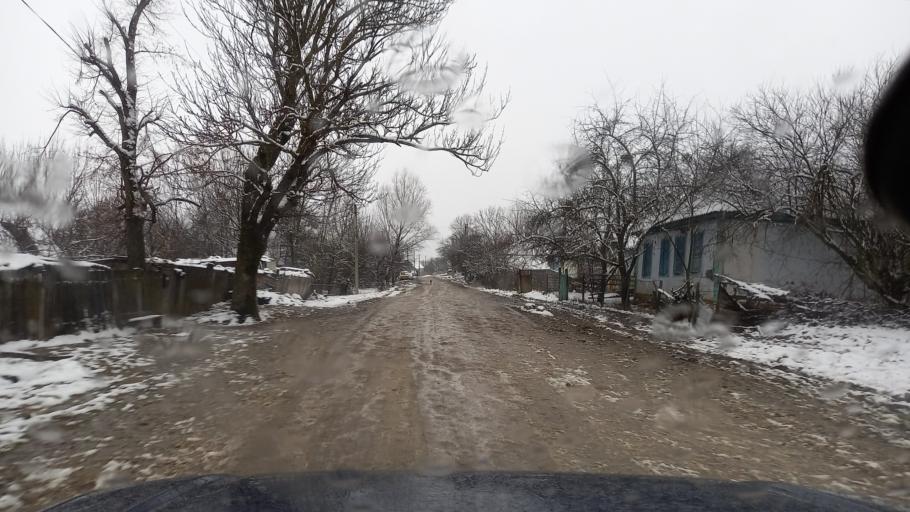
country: RU
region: Adygeya
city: Abadzekhskaya
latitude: 44.3595
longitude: 40.4095
